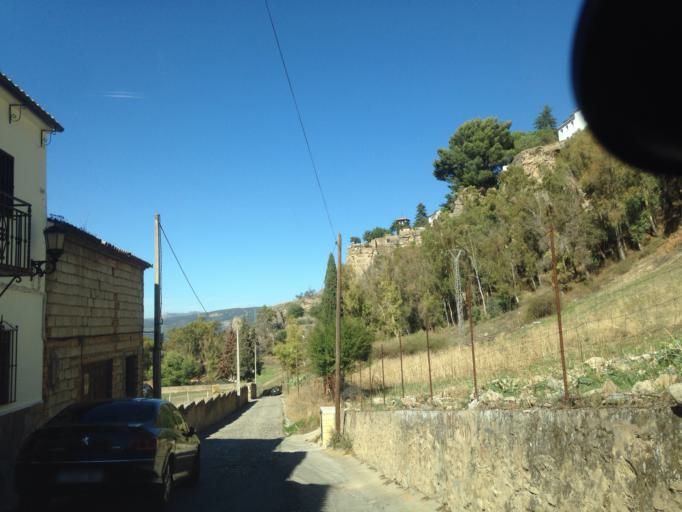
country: ES
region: Andalusia
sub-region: Provincia de Malaga
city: Ronda
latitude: 36.7352
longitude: -5.1657
